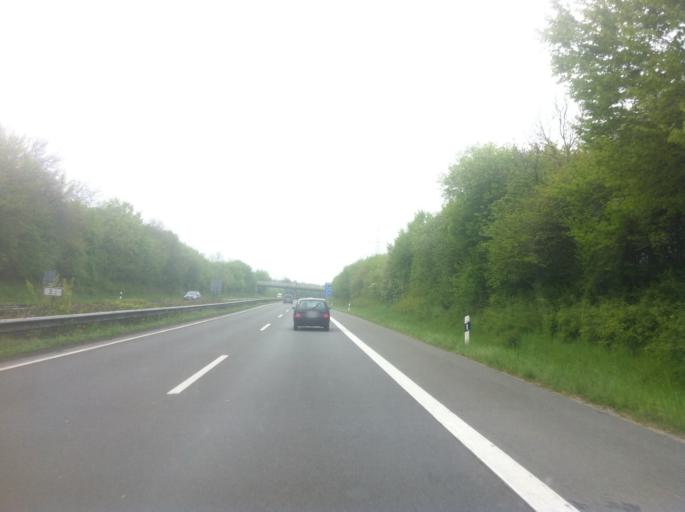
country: DE
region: North Rhine-Westphalia
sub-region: Regierungsbezirk Detmold
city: Oerlinghausen
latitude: 51.9861
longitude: 8.6402
